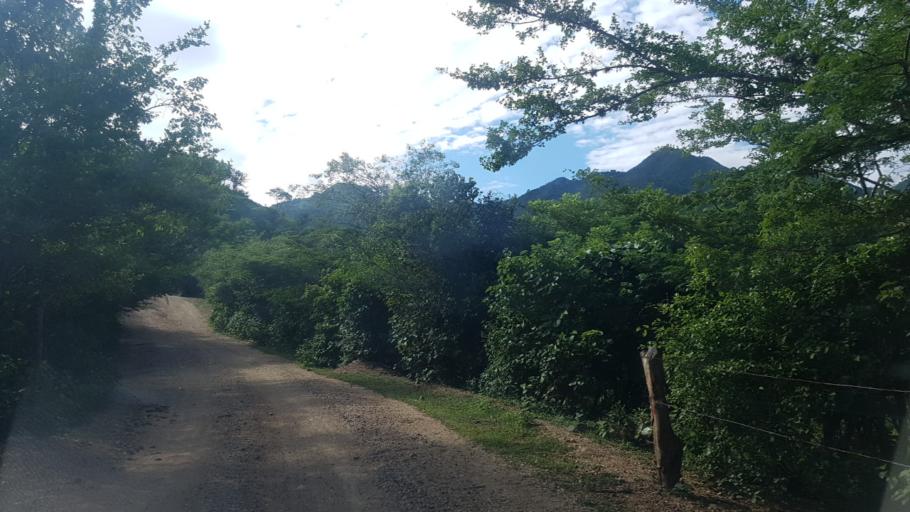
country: NI
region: Nueva Segovia
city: Ocotal
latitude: 13.6083
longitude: -86.4474
